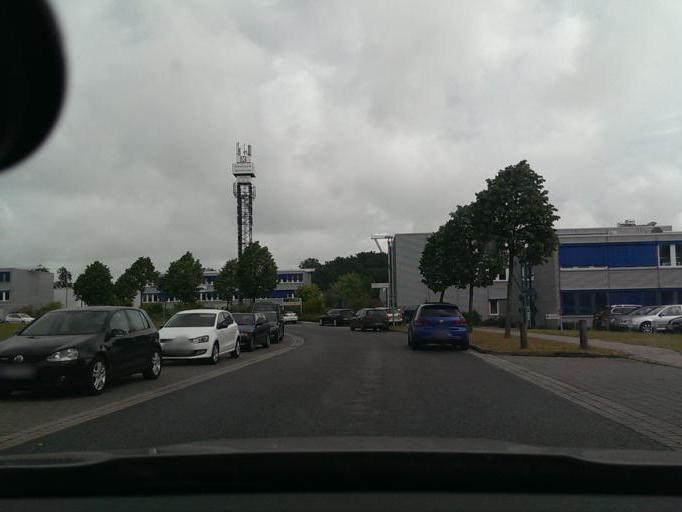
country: DE
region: Lower Saxony
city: Wolfsburg
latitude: 52.3718
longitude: 10.7425
